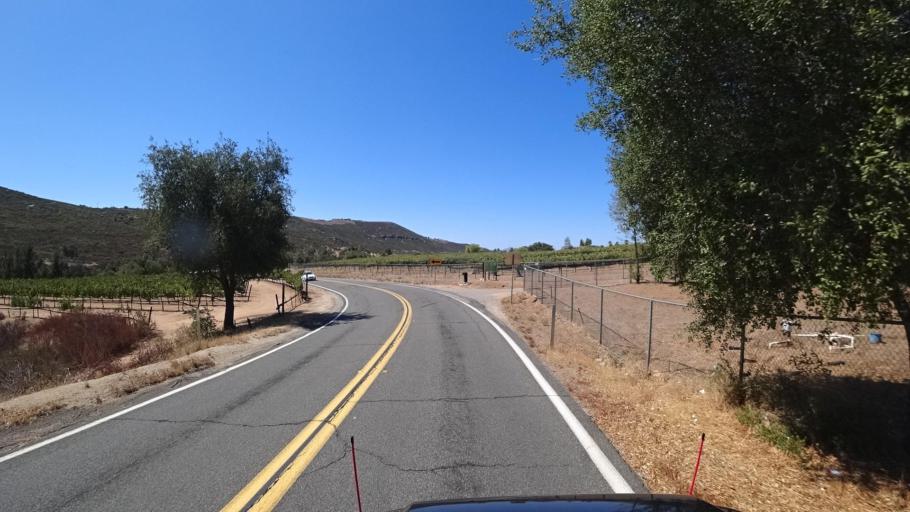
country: US
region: California
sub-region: San Diego County
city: San Diego Country Estates
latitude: 33.0521
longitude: -116.7808
